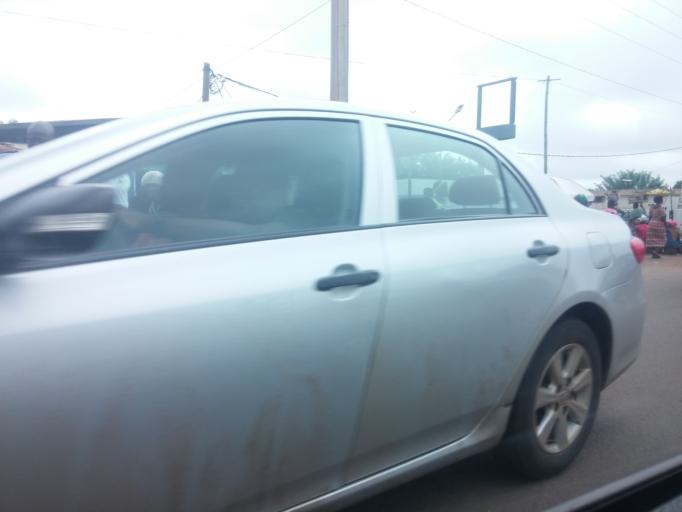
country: TG
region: Plateaux
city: Atakpame
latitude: 7.5171
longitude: 1.1472
